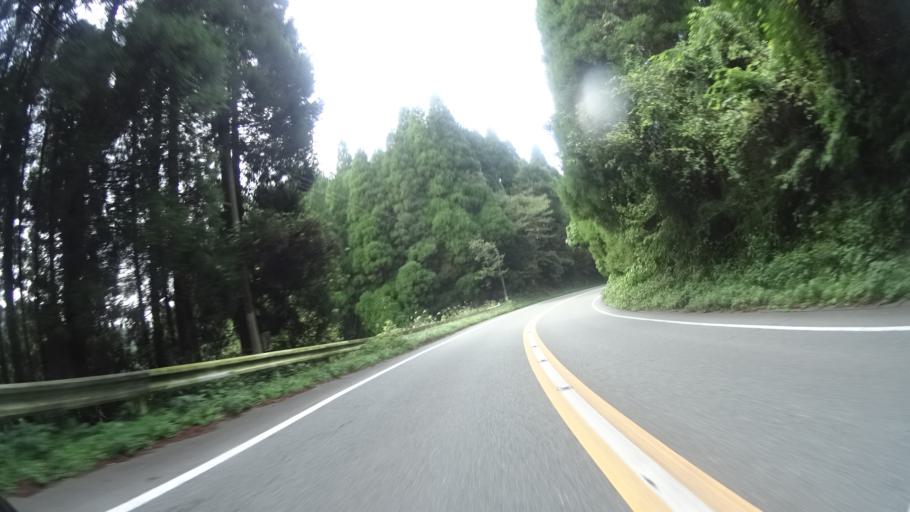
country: JP
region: Kumamoto
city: Aso
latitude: 33.0685
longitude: 131.0648
